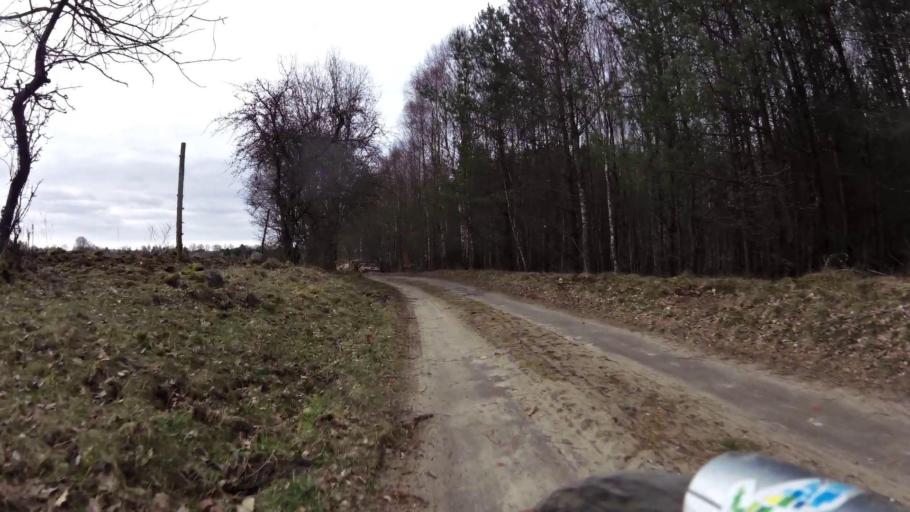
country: PL
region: Pomeranian Voivodeship
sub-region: Powiat bytowski
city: Trzebielino
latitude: 54.1113
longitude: 17.1296
